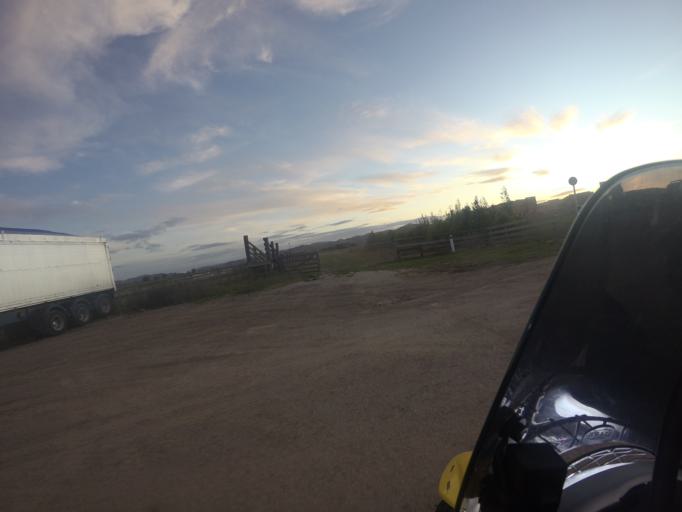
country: NZ
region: Gisborne
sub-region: Gisborne District
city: Gisborne
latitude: -38.6995
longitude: 177.9349
